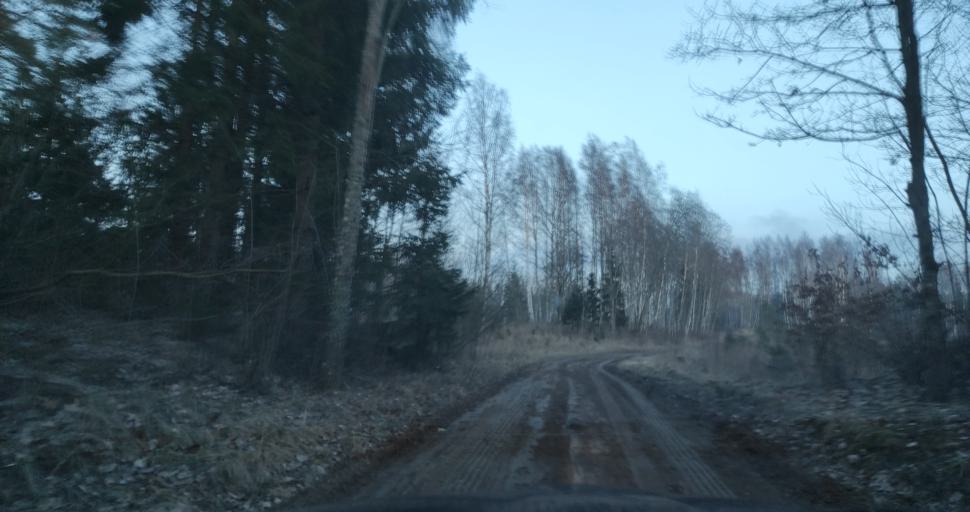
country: LV
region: Kuldigas Rajons
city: Kuldiga
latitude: 56.8133
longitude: 21.8231
